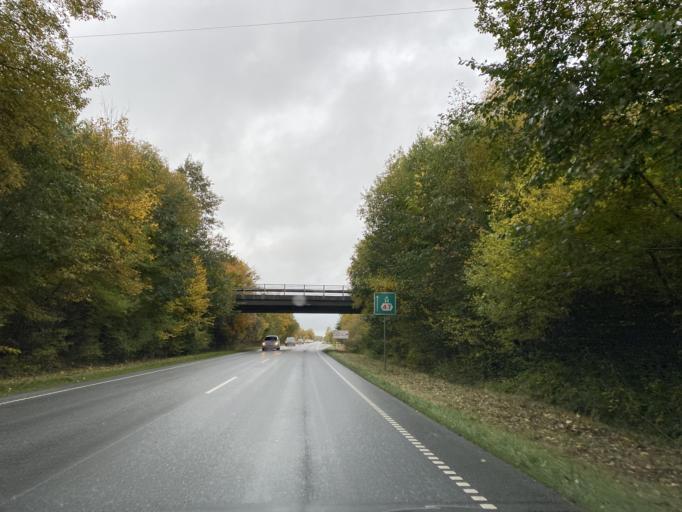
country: DK
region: Central Jutland
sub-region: Arhus Kommune
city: Framlev
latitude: 56.1852
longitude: 10.0041
